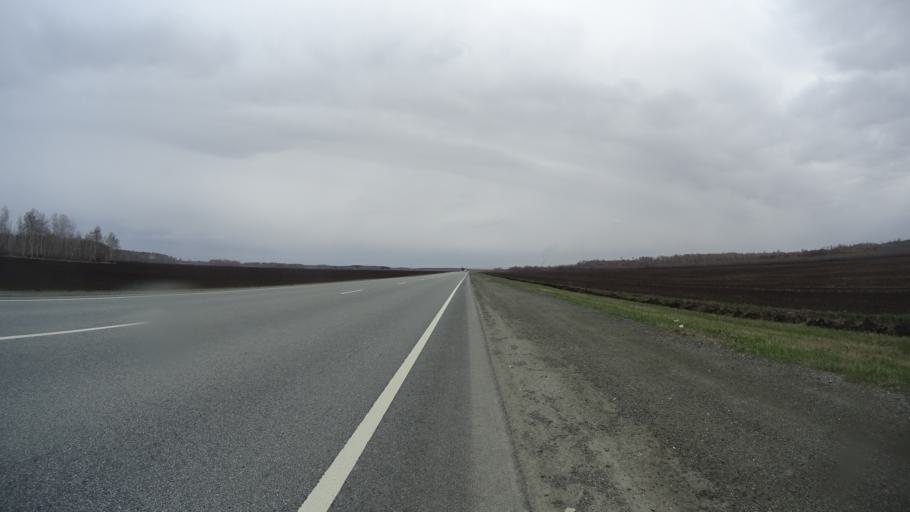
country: RU
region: Chelyabinsk
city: Krasnogorskiy
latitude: 54.5748
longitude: 61.2912
